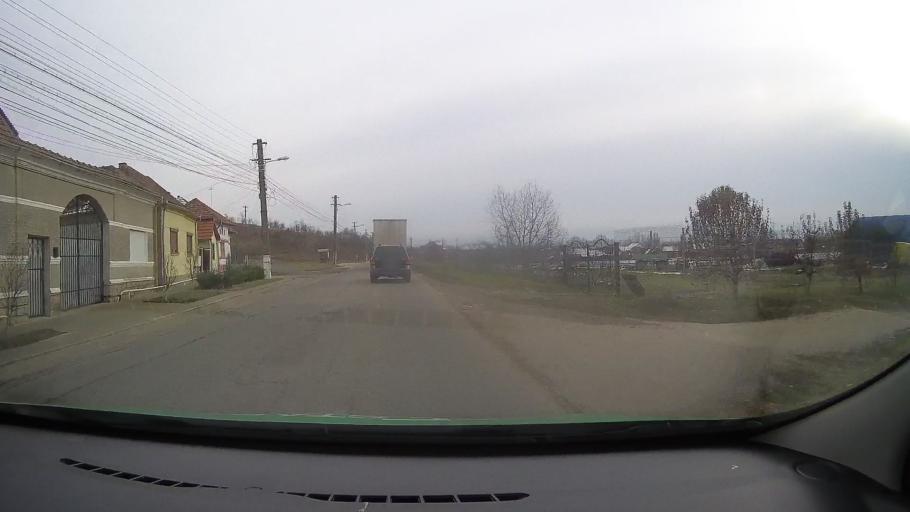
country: RO
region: Hunedoara
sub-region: Comuna Geoagiu
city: Geoagiu
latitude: 45.9081
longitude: 23.2103
